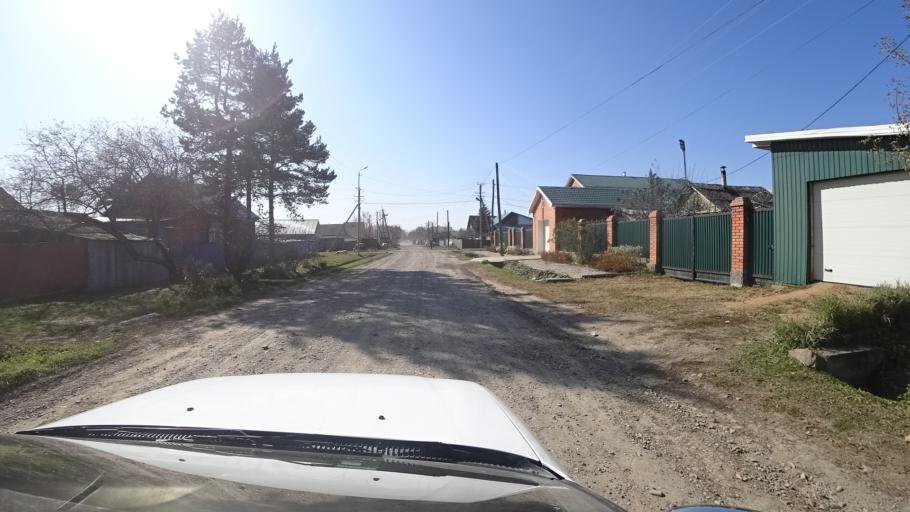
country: RU
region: Primorskiy
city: Dal'nerechensk
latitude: 45.9273
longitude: 133.7448
